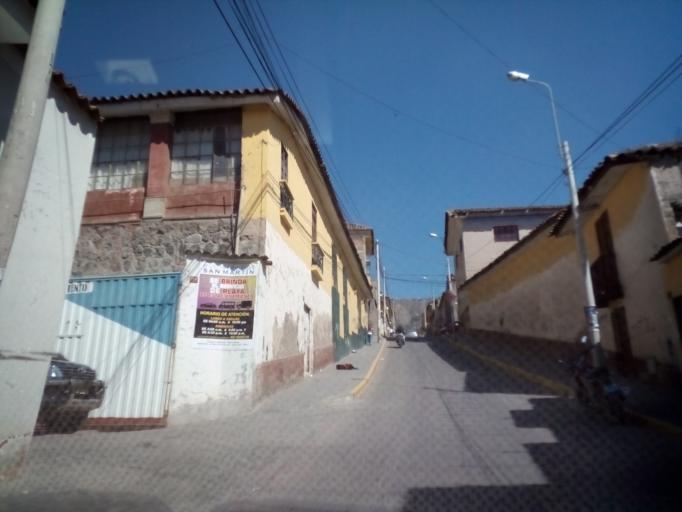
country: PE
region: Ayacucho
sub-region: Provincia de Huamanga
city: Ayacucho
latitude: -13.1626
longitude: -74.2239
